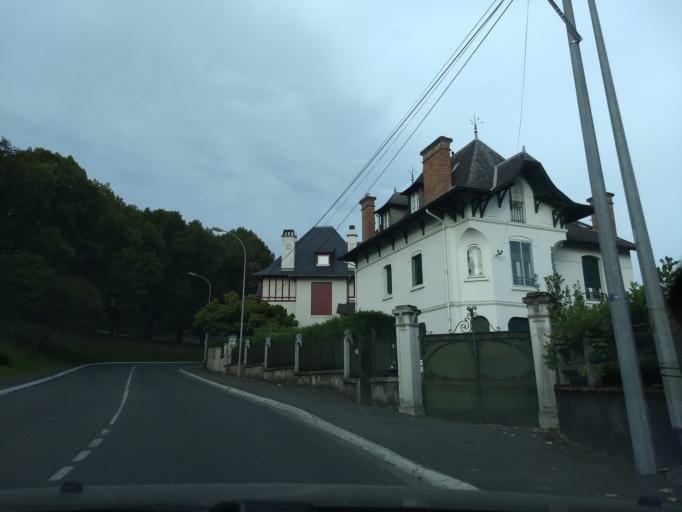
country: FR
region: Aquitaine
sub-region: Departement des Pyrenees-Atlantiques
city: Pau
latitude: 43.2945
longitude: -0.3584
